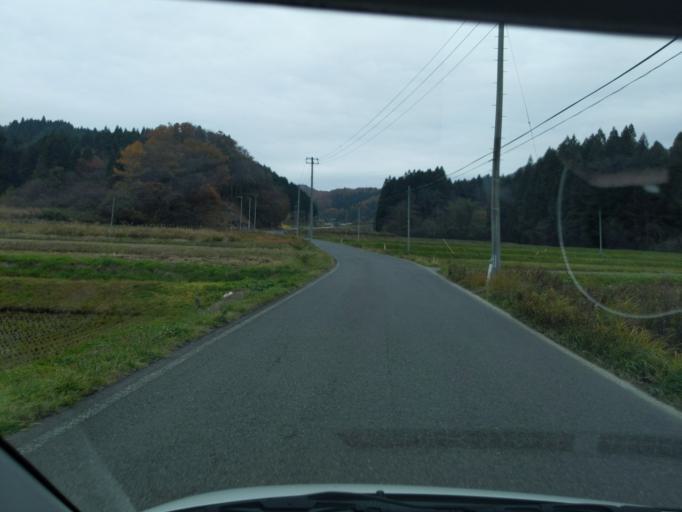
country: JP
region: Iwate
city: Kitakami
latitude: 39.2790
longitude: 141.1742
